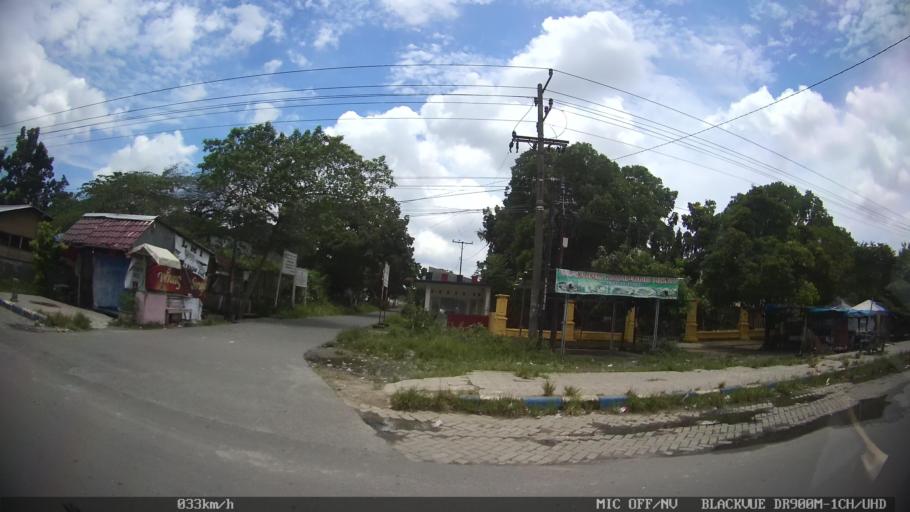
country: ID
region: North Sumatra
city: Medan
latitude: 3.6111
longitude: 98.7122
